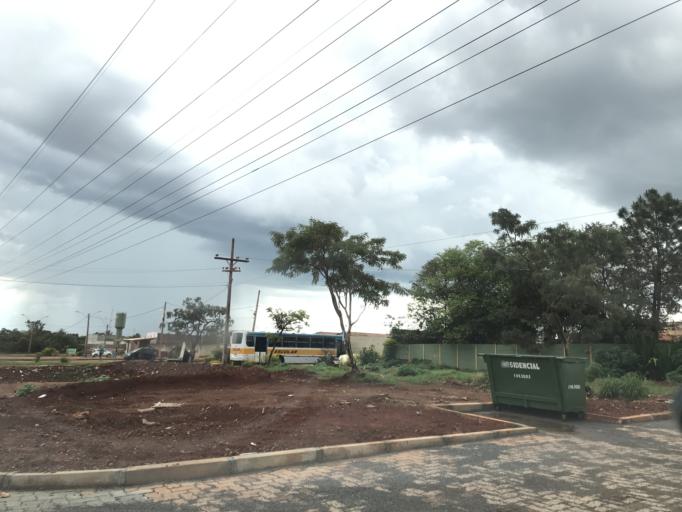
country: BR
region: Federal District
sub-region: Brasilia
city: Brasilia
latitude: -15.9692
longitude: -48.0459
